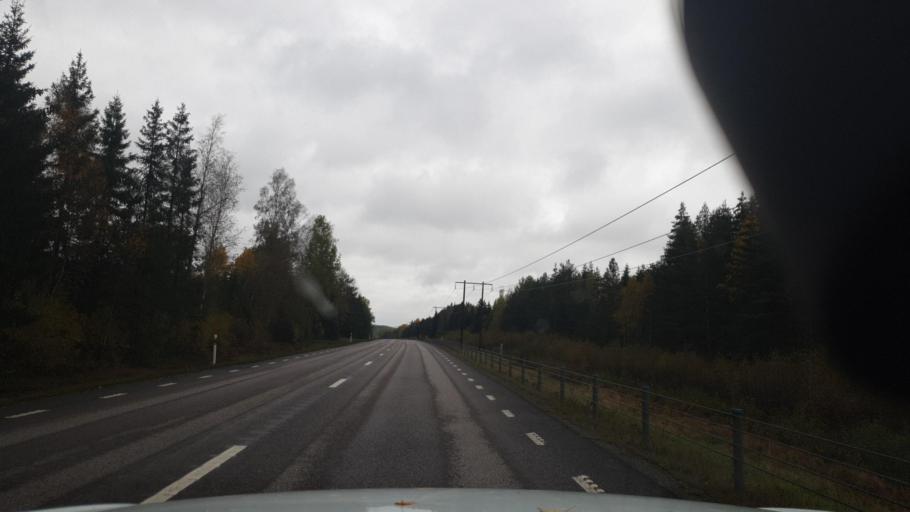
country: SE
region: Vaermland
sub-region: Karlstads Kommun
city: Edsvalla
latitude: 59.4343
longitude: 13.2007
